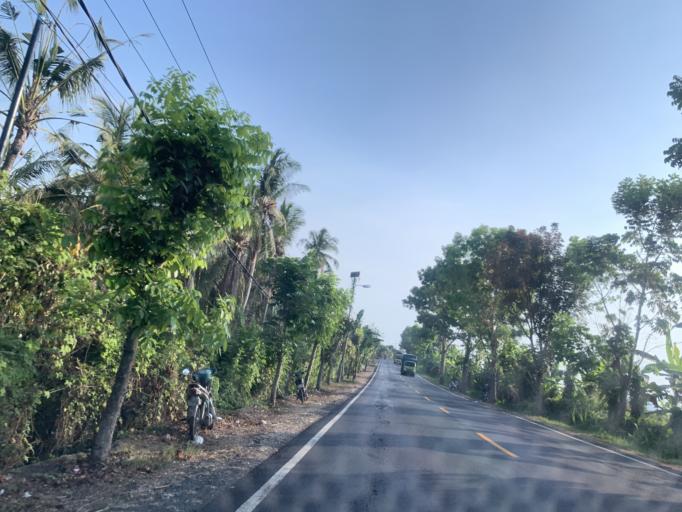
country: ID
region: Bali
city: Banjar Delodrurung
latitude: -8.5112
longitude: 115.0169
